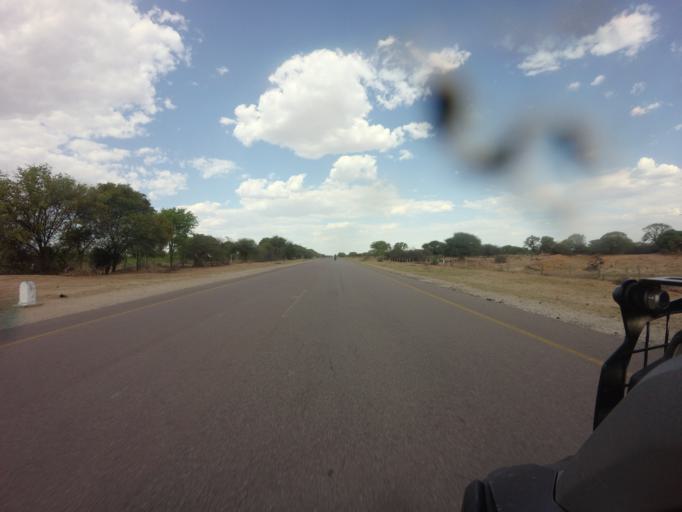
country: AO
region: Cunene
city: Ondjiva
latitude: -16.7323
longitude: 15.1629
